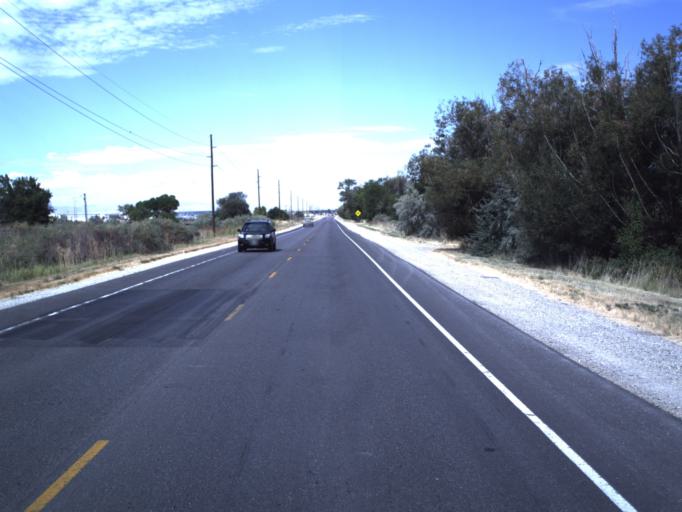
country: US
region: Utah
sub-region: Box Elder County
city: Brigham City
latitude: 41.5301
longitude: -112.0394
